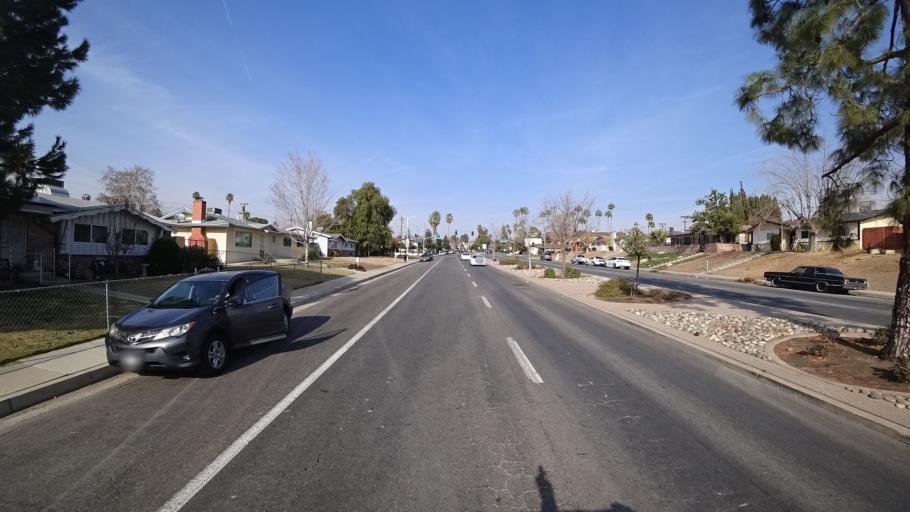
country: US
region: California
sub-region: Kern County
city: Oildale
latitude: 35.4041
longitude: -118.9499
